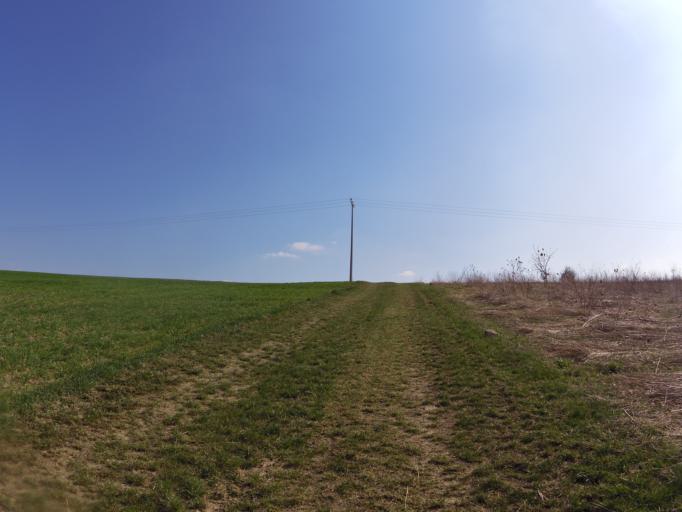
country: DE
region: Bavaria
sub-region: Regierungsbezirk Unterfranken
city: Mainstockheim
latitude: 49.8190
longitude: 10.1187
